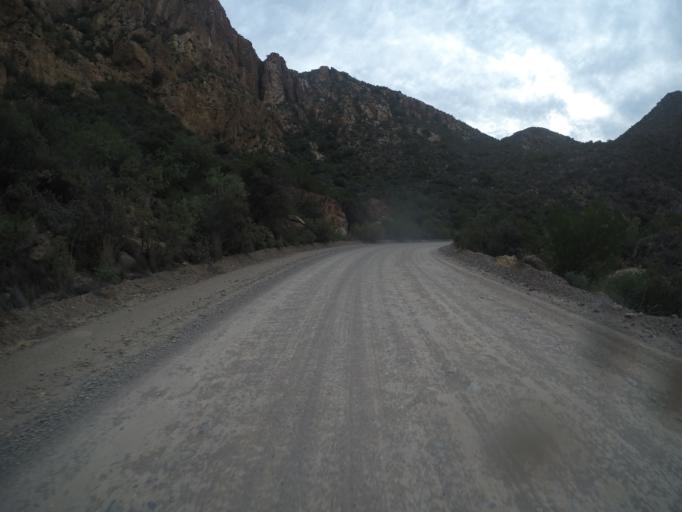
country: ZA
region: Eastern Cape
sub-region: Cacadu District Municipality
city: Willowmore
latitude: -33.5125
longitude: 23.6403
